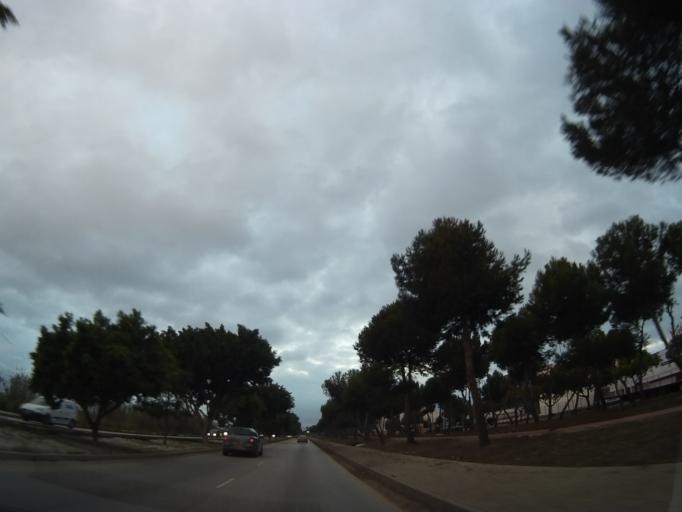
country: ES
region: Andalusia
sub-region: Provincia de Malaga
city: Malaga
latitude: 36.6875
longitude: -4.4777
